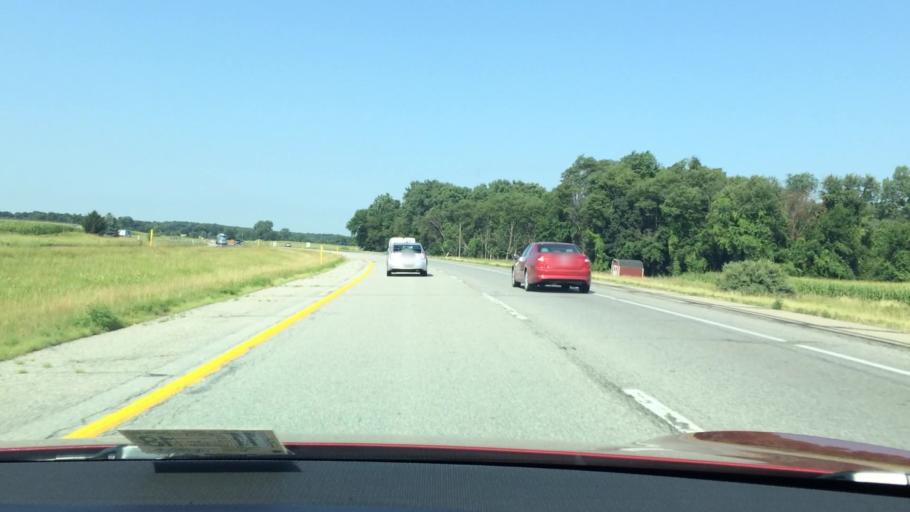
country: US
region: Michigan
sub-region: Branch County
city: Bronson
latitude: 41.7549
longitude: -85.2630
